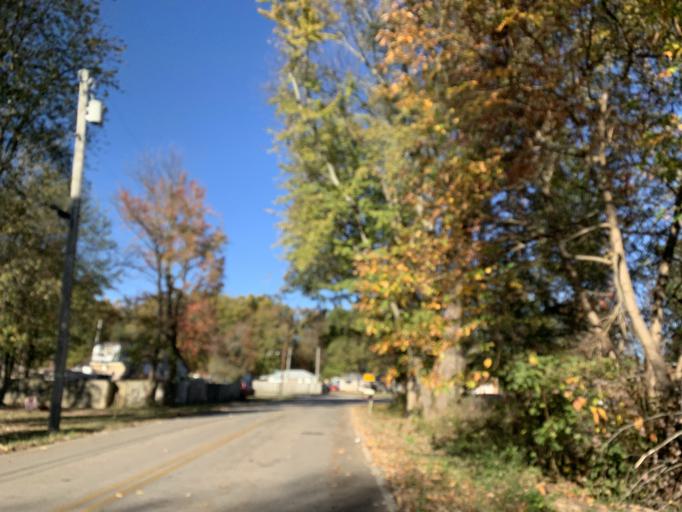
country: US
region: Kentucky
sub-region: Jefferson County
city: Pleasure Ridge Park
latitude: 38.1571
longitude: -85.8763
